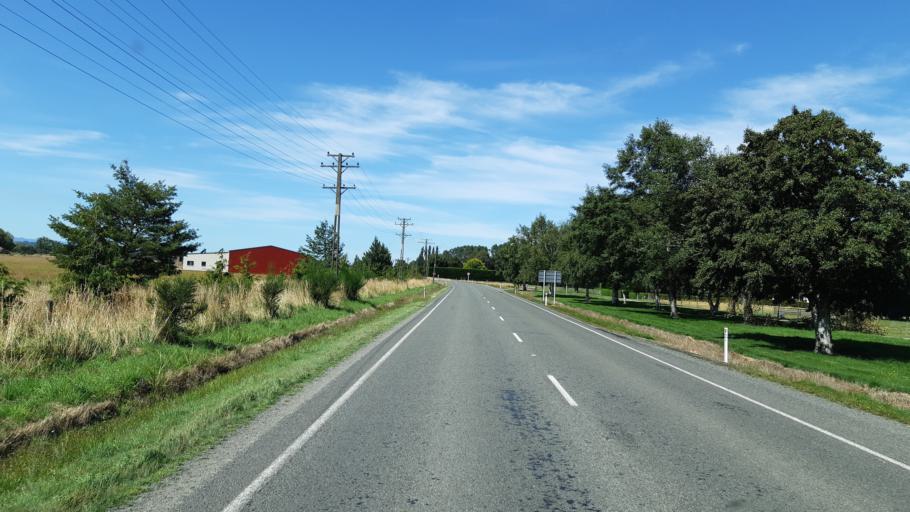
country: NZ
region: Southland
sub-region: Gore District
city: Gore
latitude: -45.9931
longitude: 168.8143
